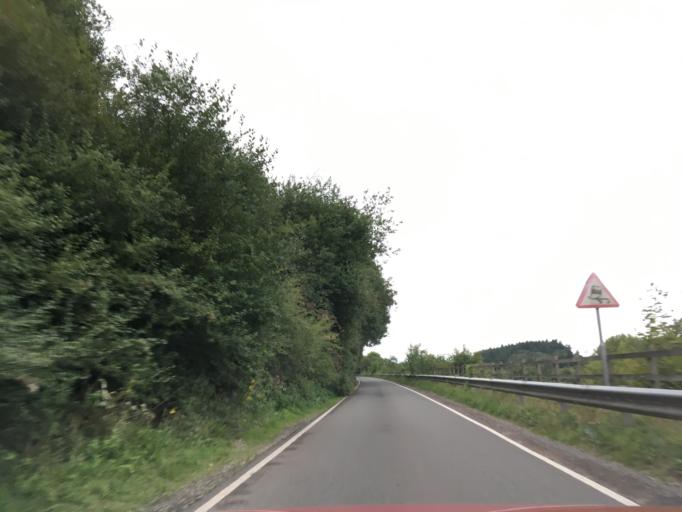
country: GB
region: Wales
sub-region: Newport
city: Langstone
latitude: 51.6222
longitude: -2.9049
